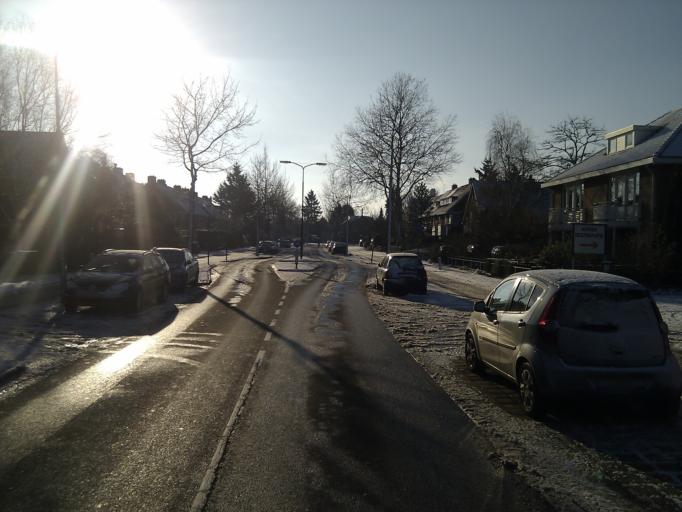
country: NL
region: Utrecht
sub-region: Gemeente De Bilt
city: De Bilt
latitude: 52.1252
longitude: 5.1951
